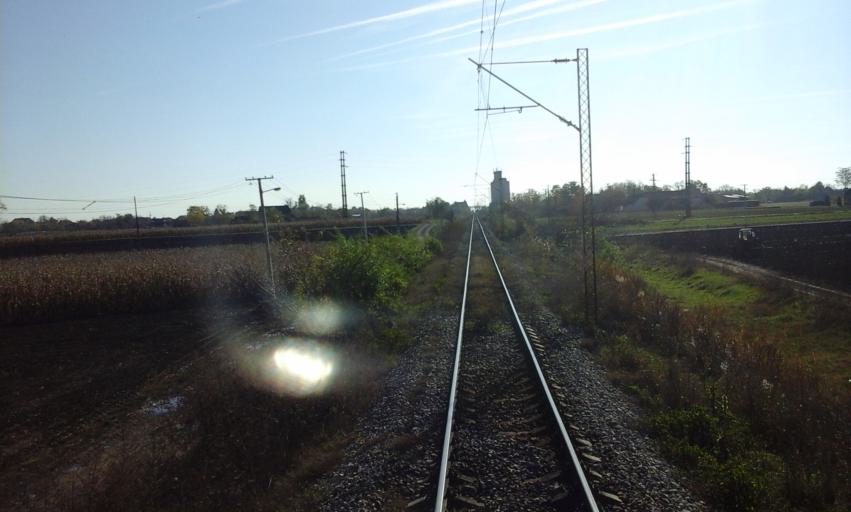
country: RS
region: Autonomna Pokrajina Vojvodina
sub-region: Severnobacki Okrug
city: Backa Topola
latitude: 45.9508
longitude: 19.6700
